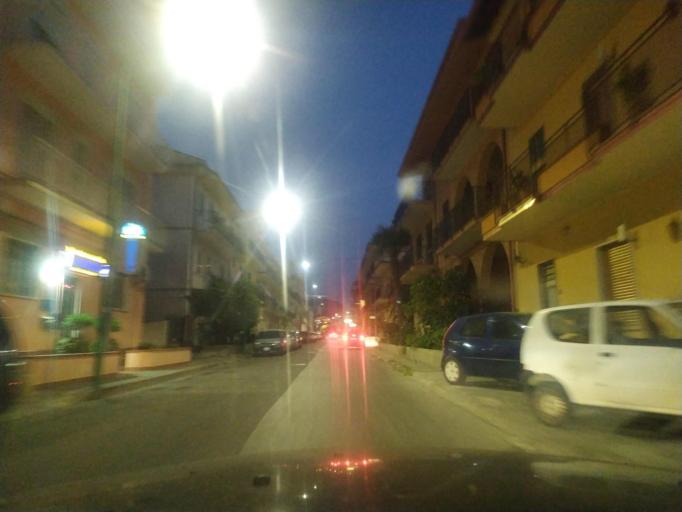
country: IT
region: Sicily
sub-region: Messina
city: Terme
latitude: 38.1391
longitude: 15.1616
